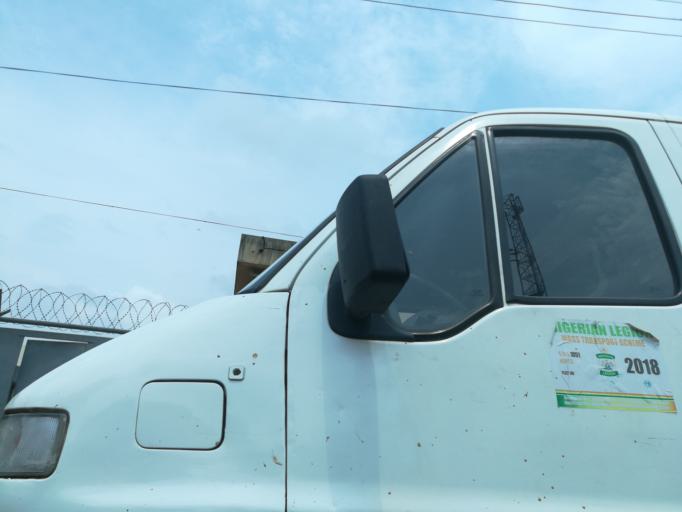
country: NG
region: Lagos
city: Oshodi
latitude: 6.5524
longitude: 3.3233
